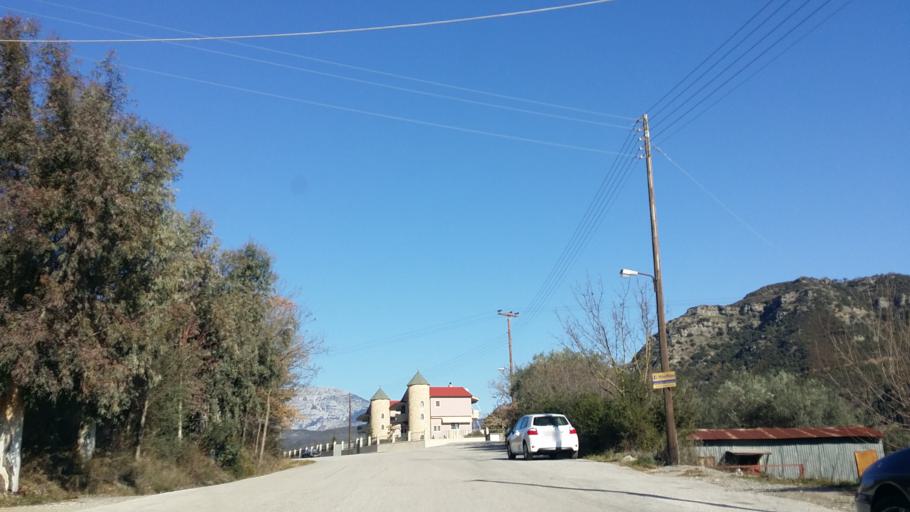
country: GR
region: West Greece
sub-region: Nomos Aitolias kai Akarnanias
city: Sardinia
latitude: 38.8967
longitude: 21.3486
